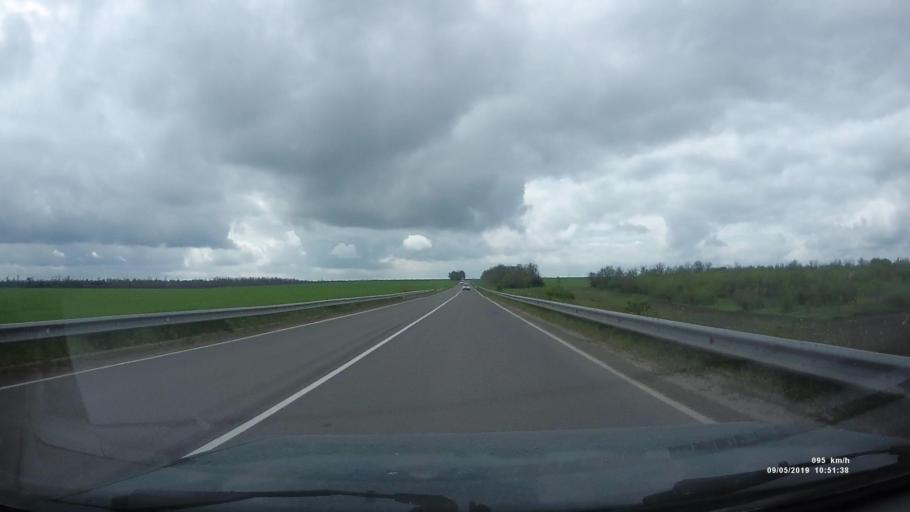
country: RU
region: Rostov
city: Peshkovo
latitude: 46.9122
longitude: 39.3551
